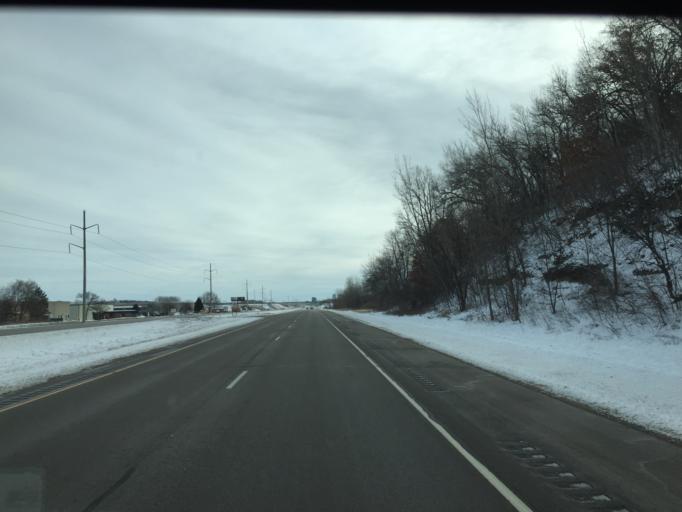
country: US
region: Minnesota
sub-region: Olmsted County
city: Rochester
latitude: 44.0397
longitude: -92.5311
